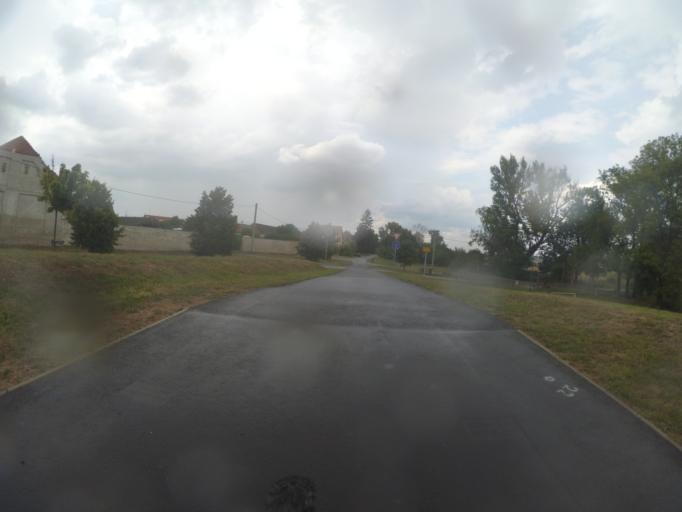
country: CZ
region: Central Bohemia
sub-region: Okres Melnik
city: Melnik
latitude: 50.3234
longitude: 14.4537
